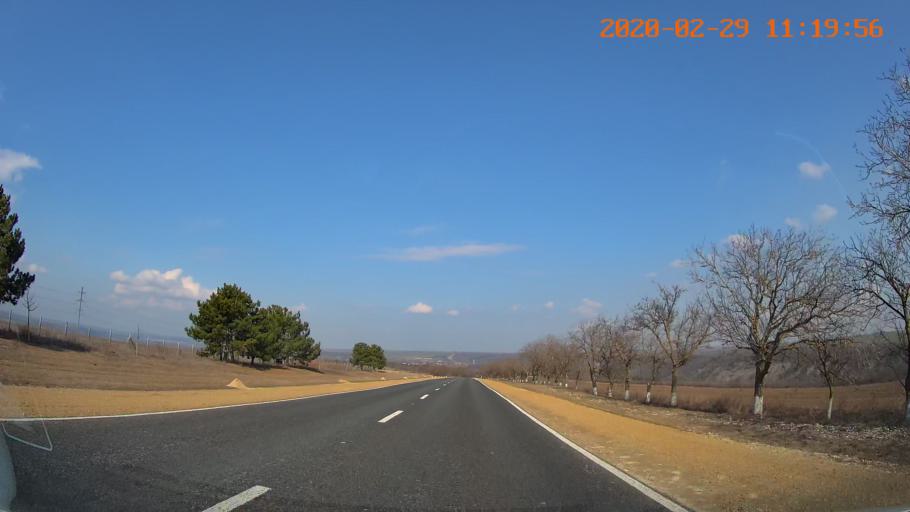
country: MD
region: Telenesti
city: Cocieri
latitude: 47.3577
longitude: 29.1729
